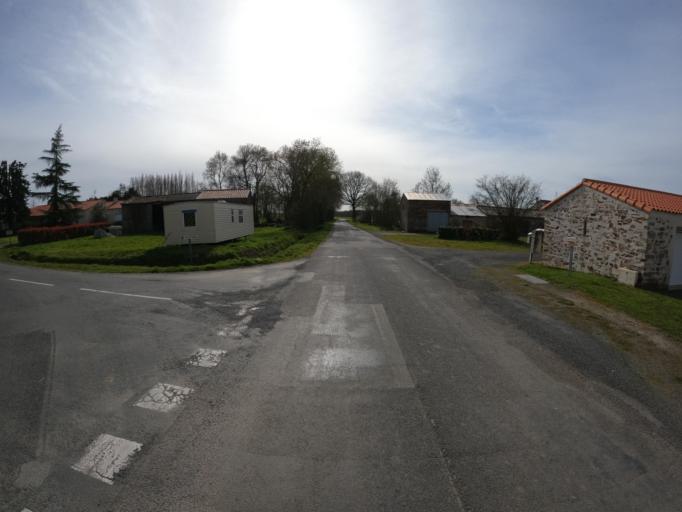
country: FR
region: Pays de la Loire
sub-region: Departement de la Vendee
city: Bouffere
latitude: 46.9523
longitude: -1.3696
